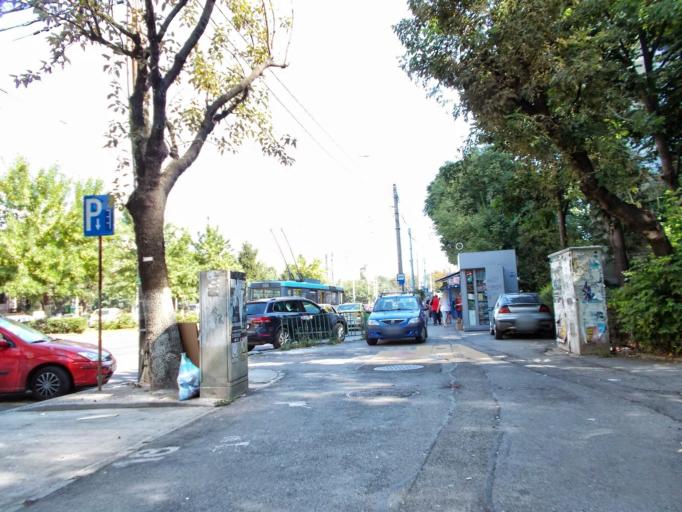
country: RO
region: Bucuresti
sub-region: Municipiul Bucuresti
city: Bucuresti
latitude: 44.3882
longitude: 26.1180
